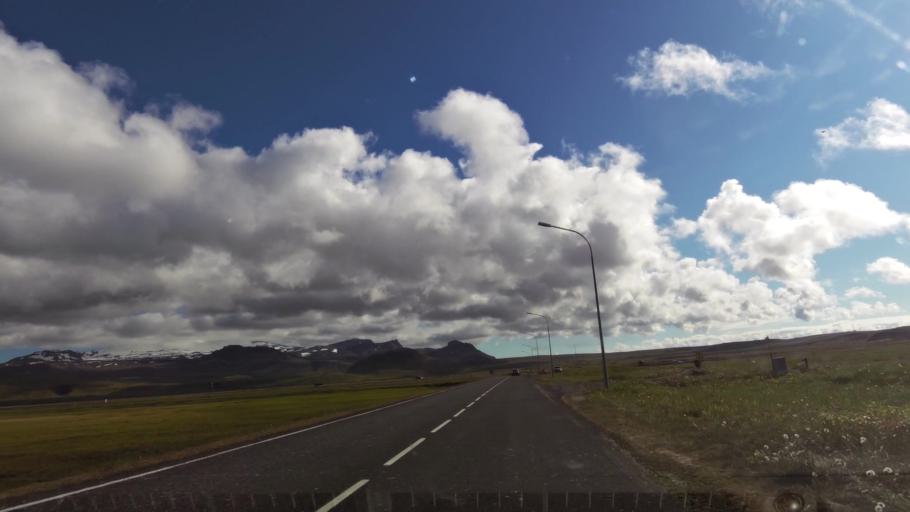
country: IS
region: West
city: Olafsvik
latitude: 64.9210
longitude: -23.8185
